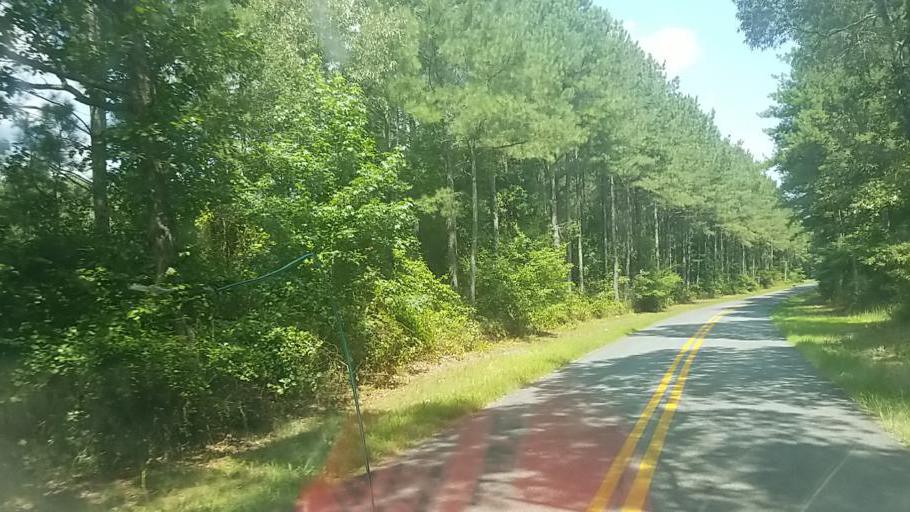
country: US
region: Maryland
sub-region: Worcester County
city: Snow Hill
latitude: 38.2781
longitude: -75.4748
